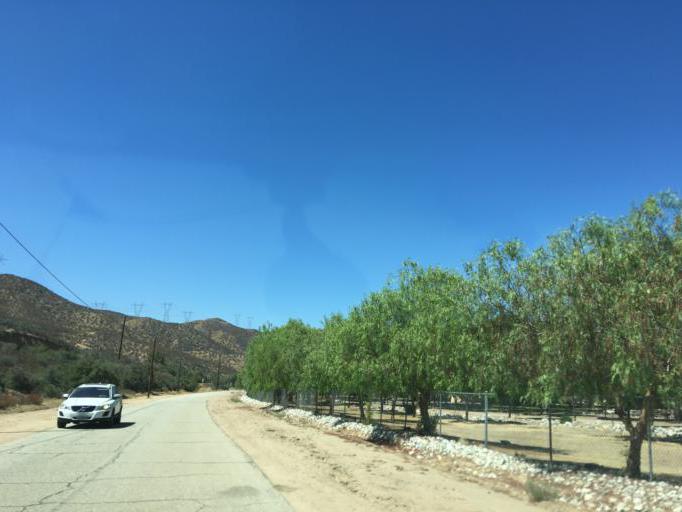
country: US
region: California
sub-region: Los Angeles County
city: Agua Dulce
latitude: 34.5149
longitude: -118.3377
